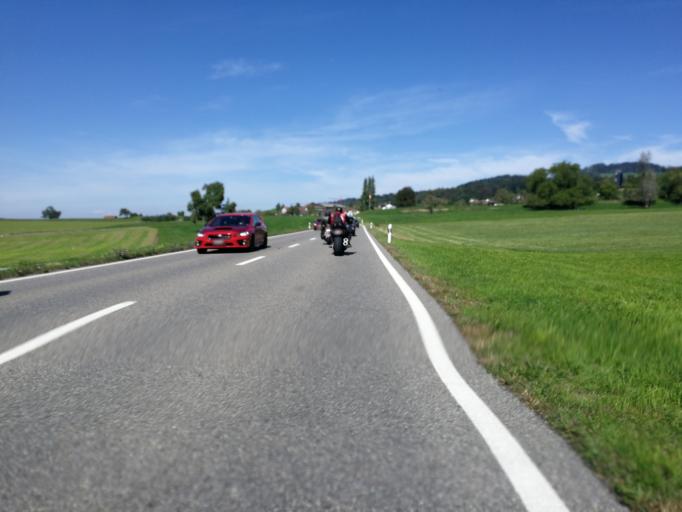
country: CH
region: Zurich
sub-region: Bezirk Hinwil
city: Wetzikon / Kempten
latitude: 47.3181
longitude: 8.8262
